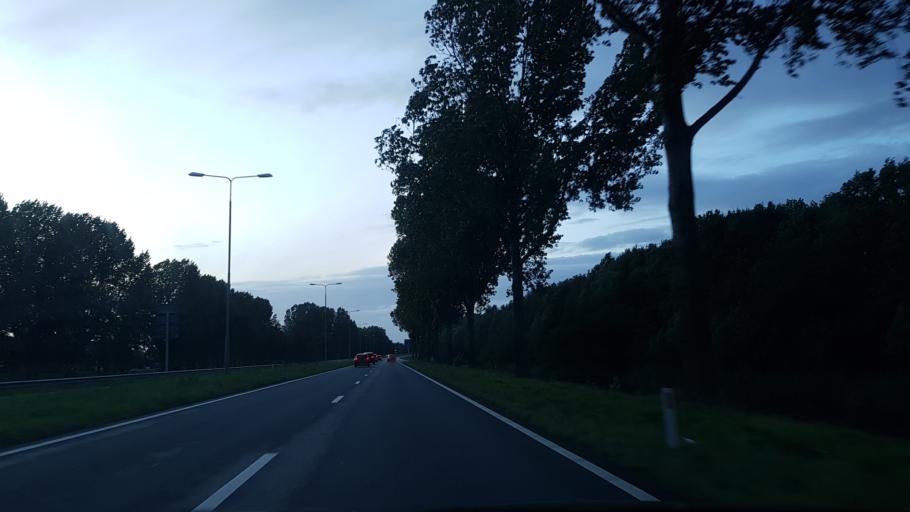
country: NL
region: North Holland
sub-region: Gemeente Heemstede
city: Heemstede
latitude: 52.3324
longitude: 4.6438
